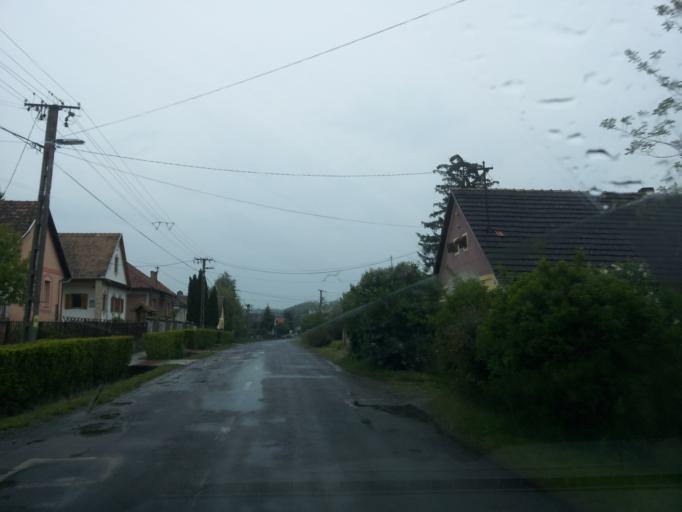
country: HU
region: Tolna
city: Szentgalpuszta
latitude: 46.2794
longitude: 18.6422
